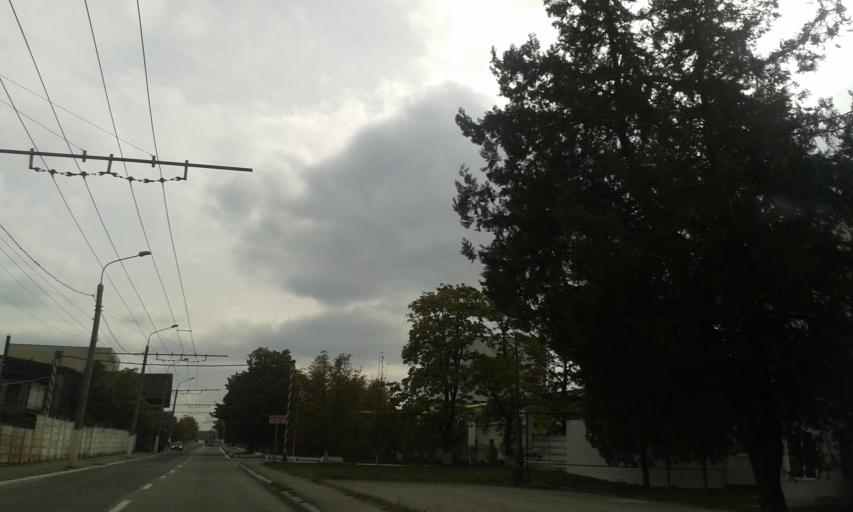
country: RO
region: Gorj
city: Targu Jiu
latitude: 45.0711
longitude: 23.3072
